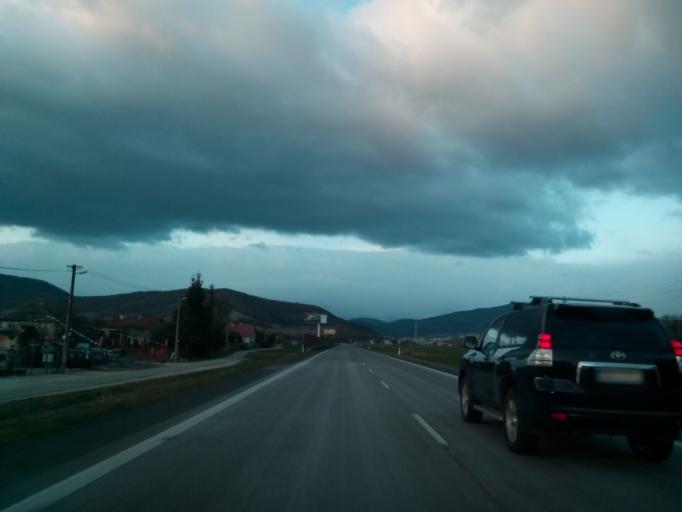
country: SK
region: Kosicky
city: Roznava
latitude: 48.6287
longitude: 20.5030
